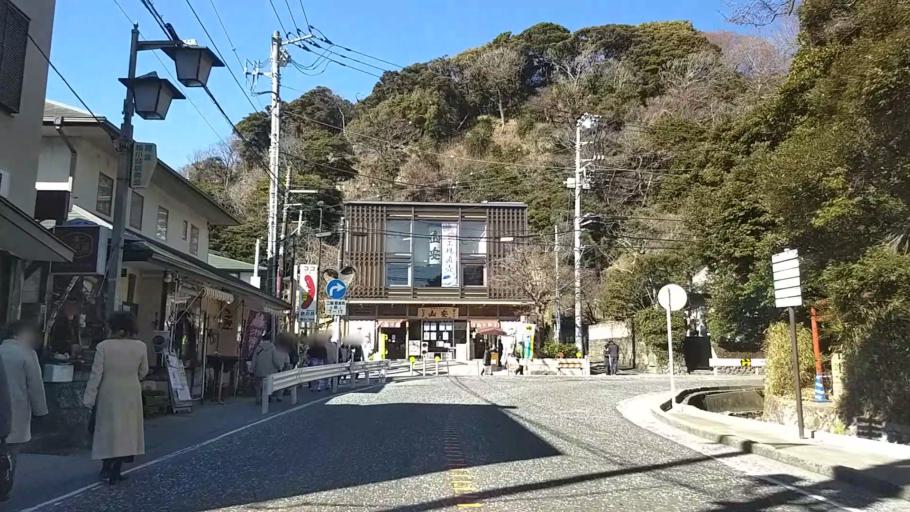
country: JP
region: Kanagawa
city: Kamakura
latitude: 35.3241
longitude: 139.5541
